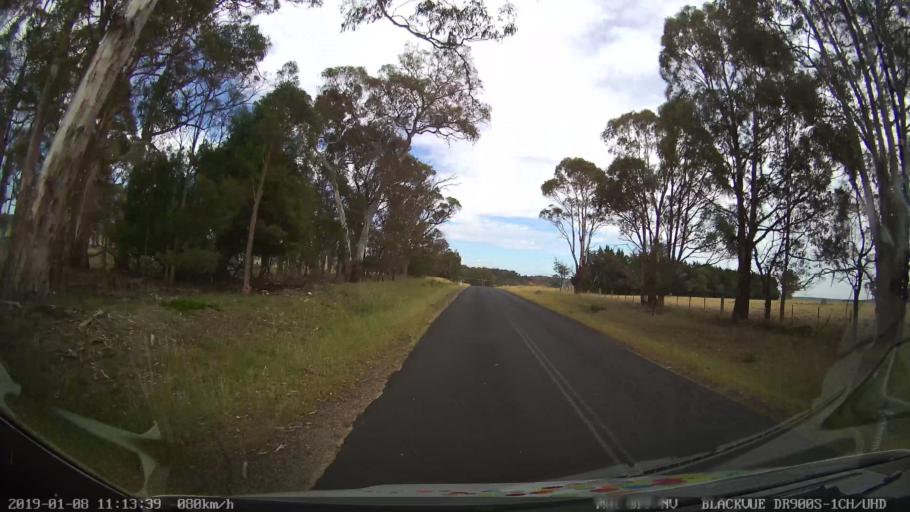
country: AU
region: New South Wales
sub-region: Guyra
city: Guyra
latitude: -30.2292
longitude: 151.5978
